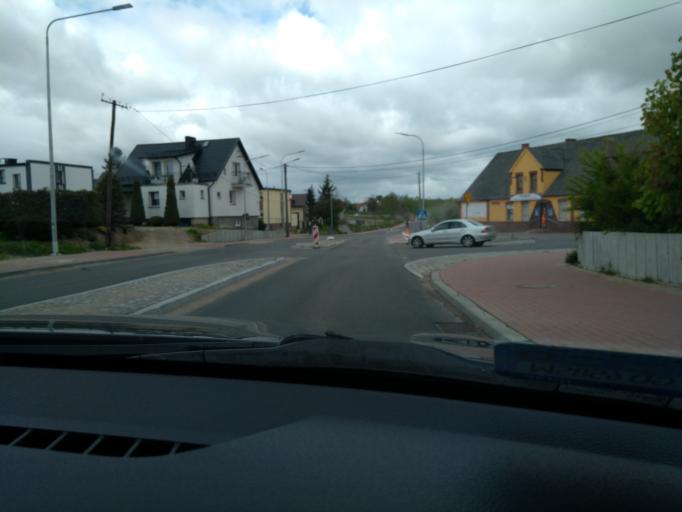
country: PL
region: Pomeranian Voivodeship
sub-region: Powiat kartuski
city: Garcz
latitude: 54.3462
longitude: 18.1302
